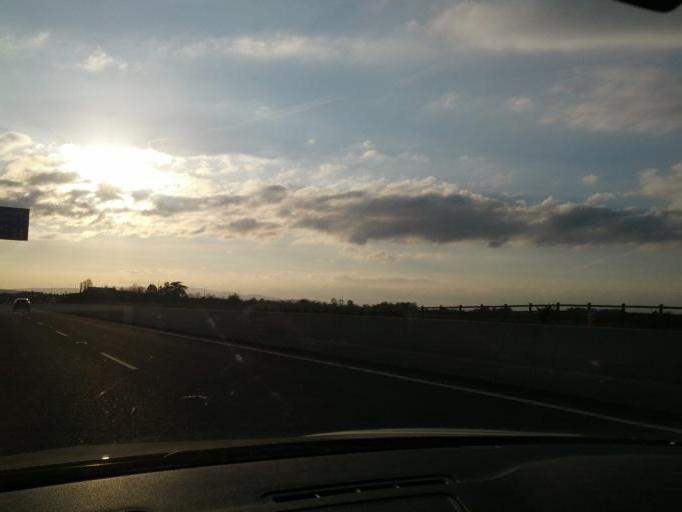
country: IE
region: Munster
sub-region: North Tipperary
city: Nenagh
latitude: 52.8616
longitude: -8.1107
